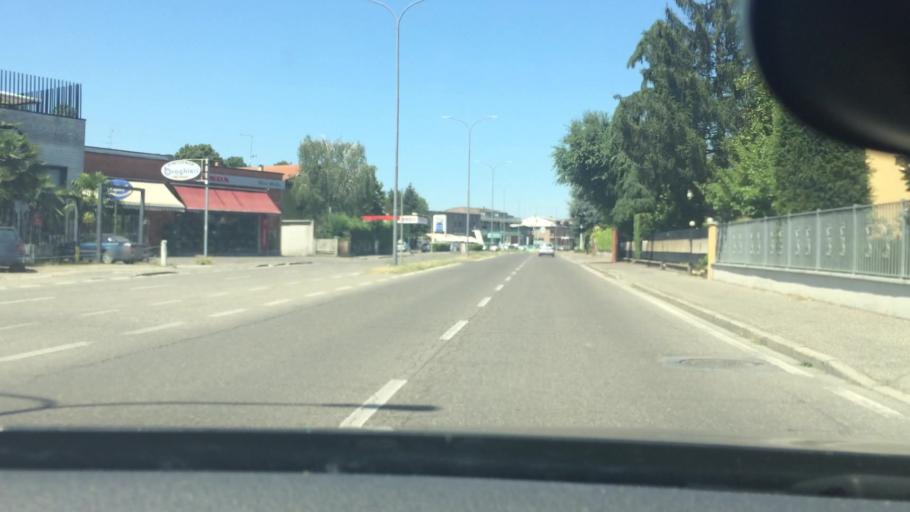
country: IT
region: Emilia-Romagna
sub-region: Provincia di Piacenza
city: Piacenza
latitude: 45.0475
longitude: 9.6668
